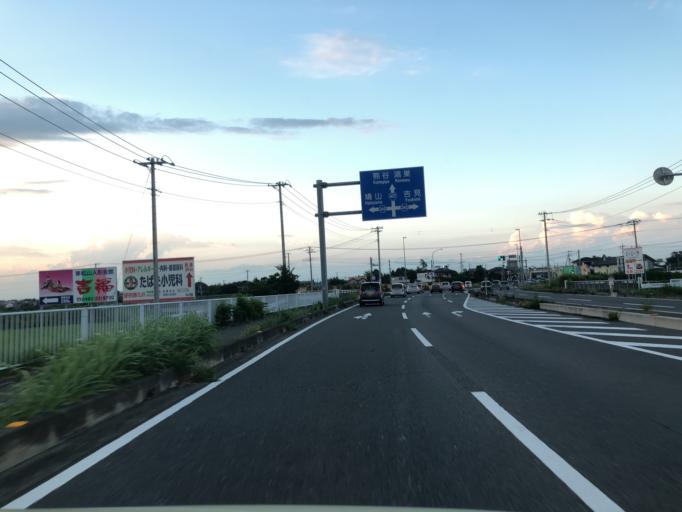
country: JP
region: Saitama
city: Sakado
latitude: 36.0165
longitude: 139.4097
